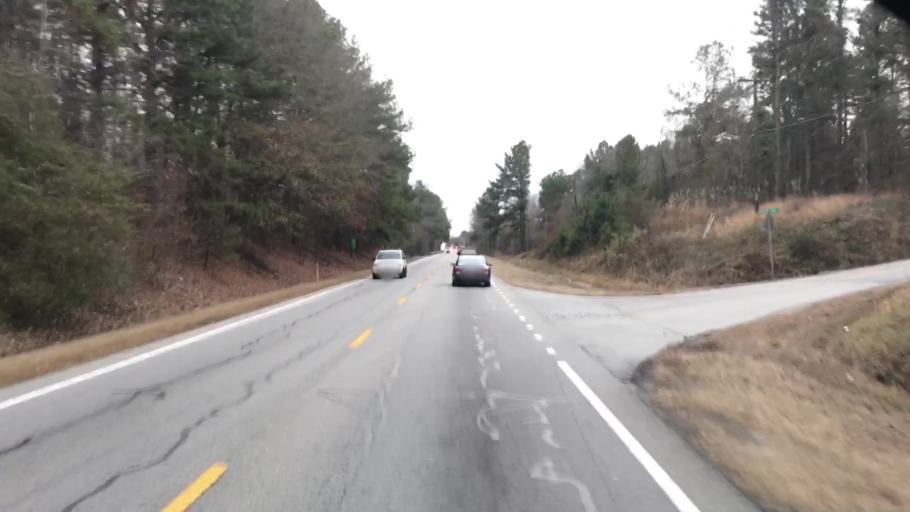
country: US
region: Georgia
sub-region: Jackson County
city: Hoschton
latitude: 34.0756
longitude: -83.7902
